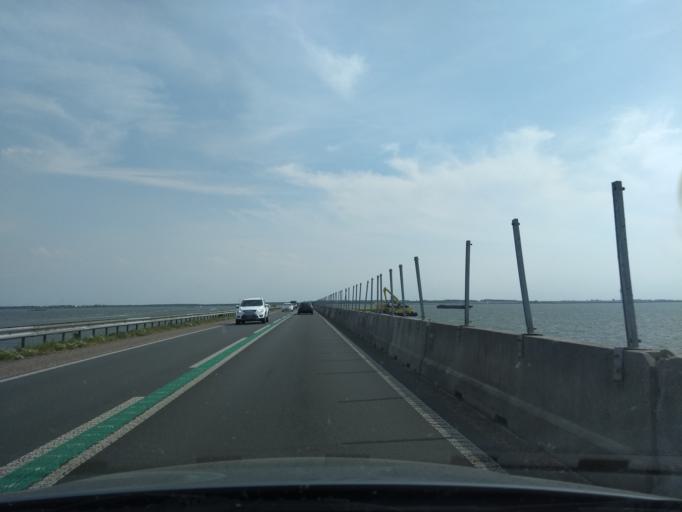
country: NL
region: Flevoland
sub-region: Gemeente Lelystad
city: Lelystad
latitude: 52.5828
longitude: 5.4618
